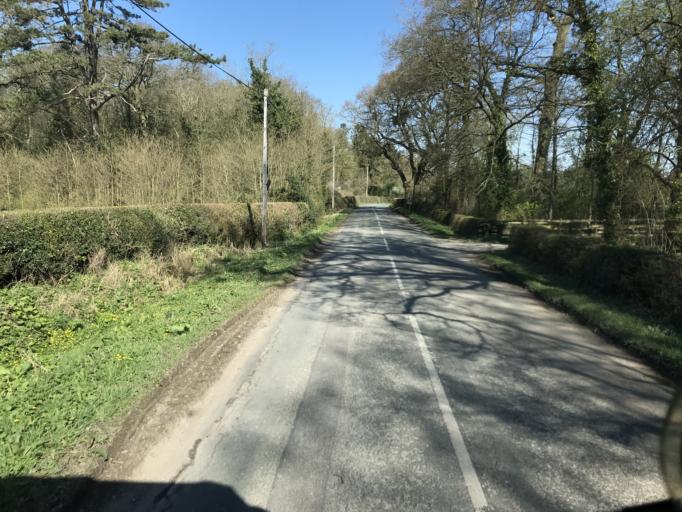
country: GB
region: England
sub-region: Cheshire West and Chester
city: Aldford
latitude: 53.1409
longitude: -2.8423
